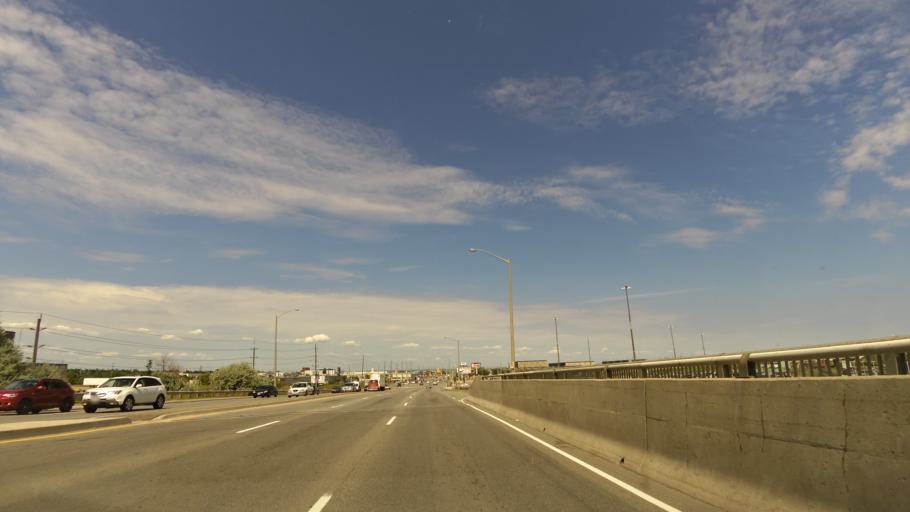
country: CA
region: Ontario
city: Brampton
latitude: 43.7012
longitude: -79.6943
